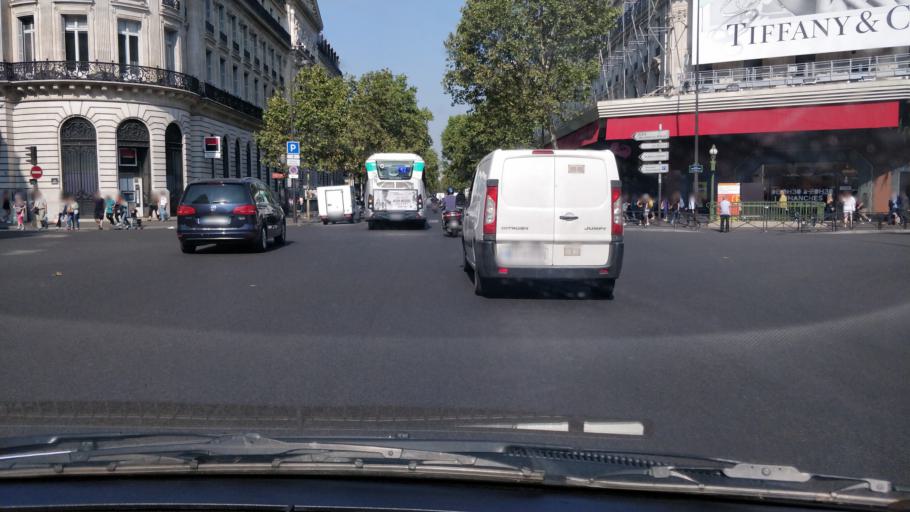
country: FR
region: Ile-de-France
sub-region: Paris
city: Paris
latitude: 48.8730
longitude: 2.3335
